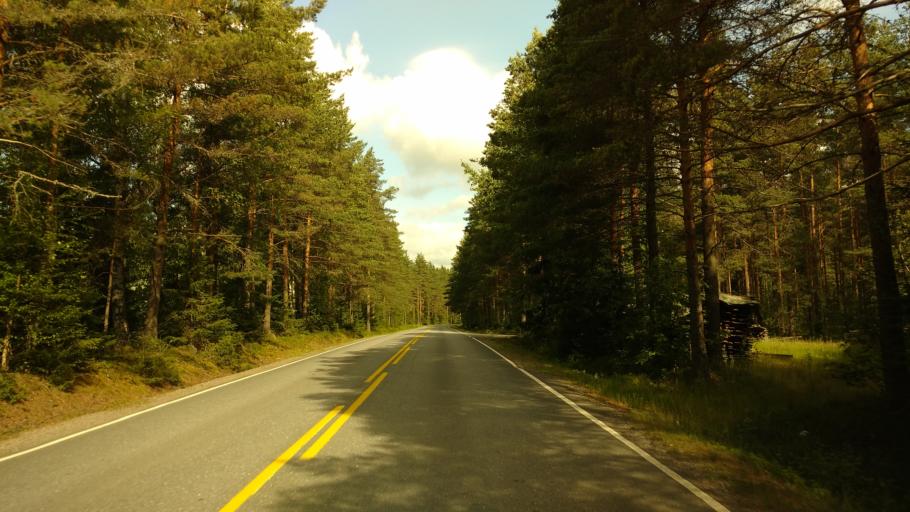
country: FI
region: Varsinais-Suomi
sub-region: Loimaa
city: Koski Tl
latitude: 60.6272
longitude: 23.1094
